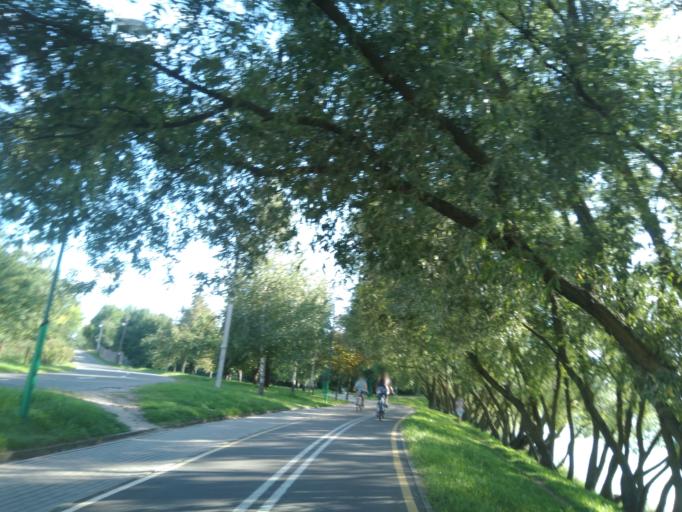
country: BY
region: Minsk
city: Minsk
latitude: 53.8812
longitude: 27.5756
